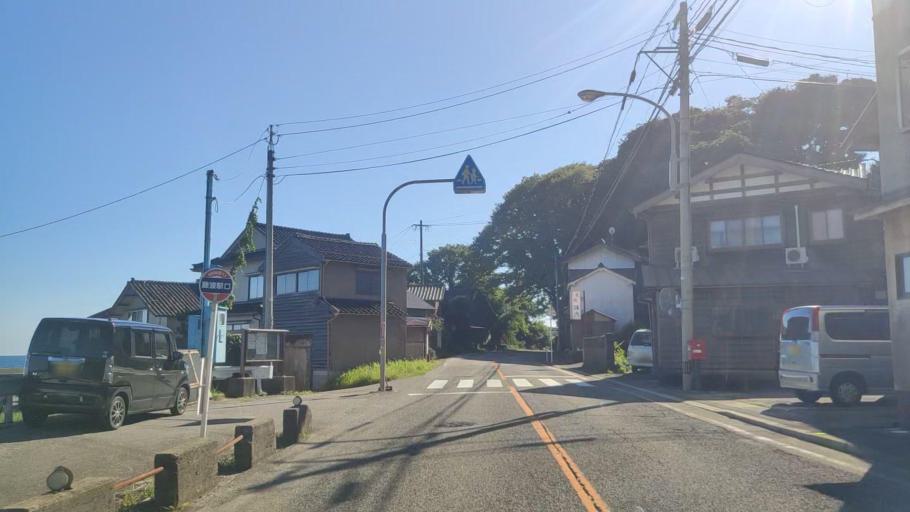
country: JP
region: Ishikawa
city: Nanao
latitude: 37.2951
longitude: 137.1366
